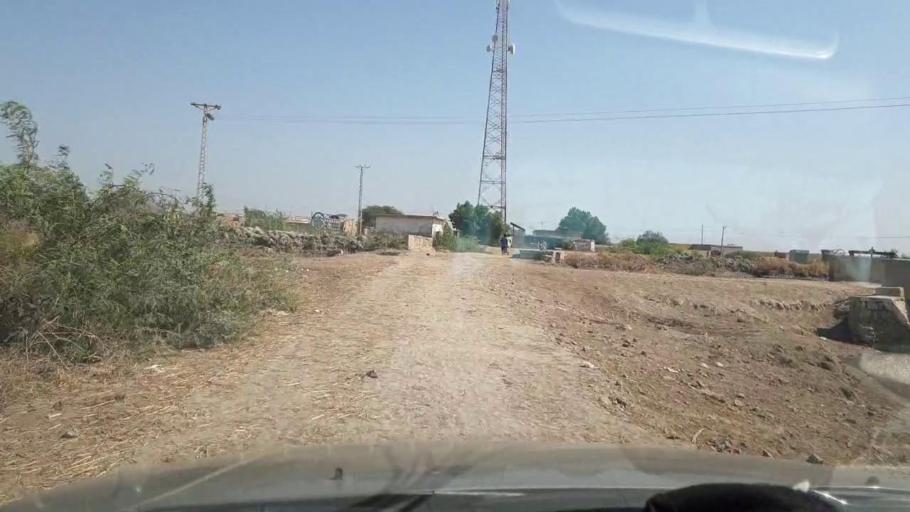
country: PK
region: Sindh
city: Daro Mehar
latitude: 24.9684
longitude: 68.1208
